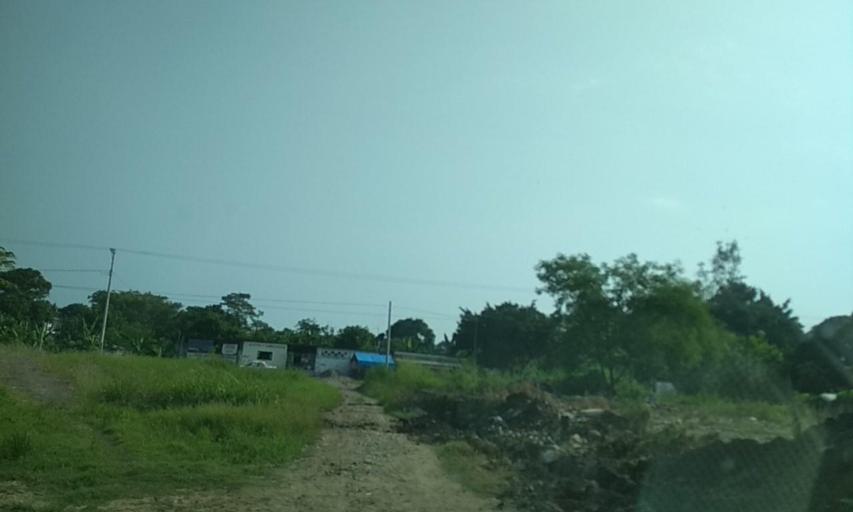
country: MX
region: Veracruz
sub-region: Atzalan
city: Colonias Pedernales
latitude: 20.0515
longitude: -96.9909
